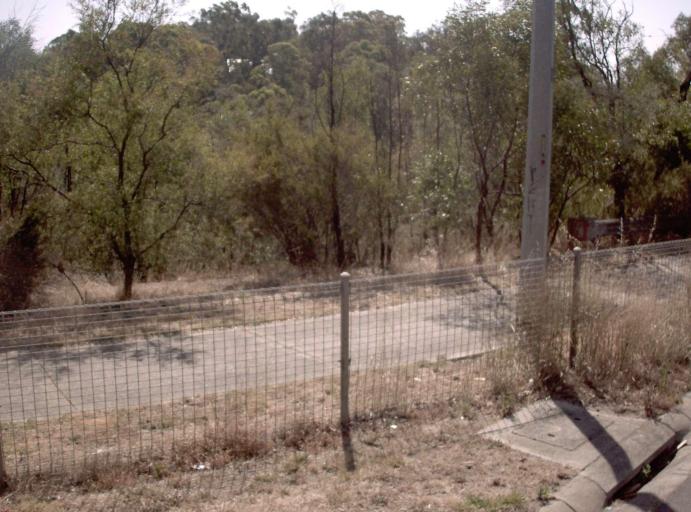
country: AU
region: Victoria
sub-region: Nillumbik
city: Eltham
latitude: -37.7415
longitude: 145.1360
